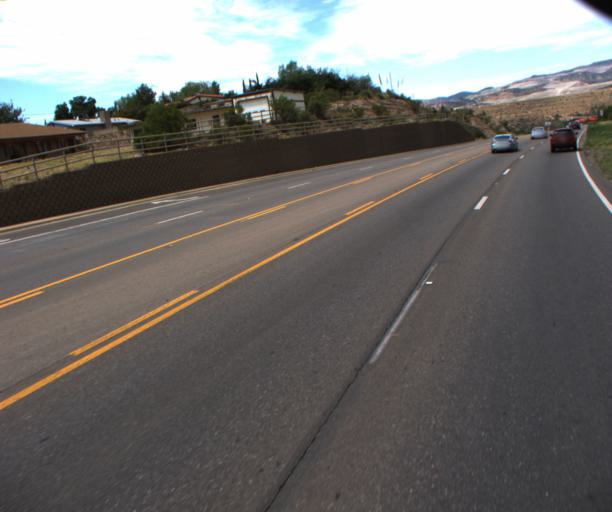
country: US
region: Arizona
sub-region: Gila County
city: Central Heights-Midland City
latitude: 33.4185
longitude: -110.8196
